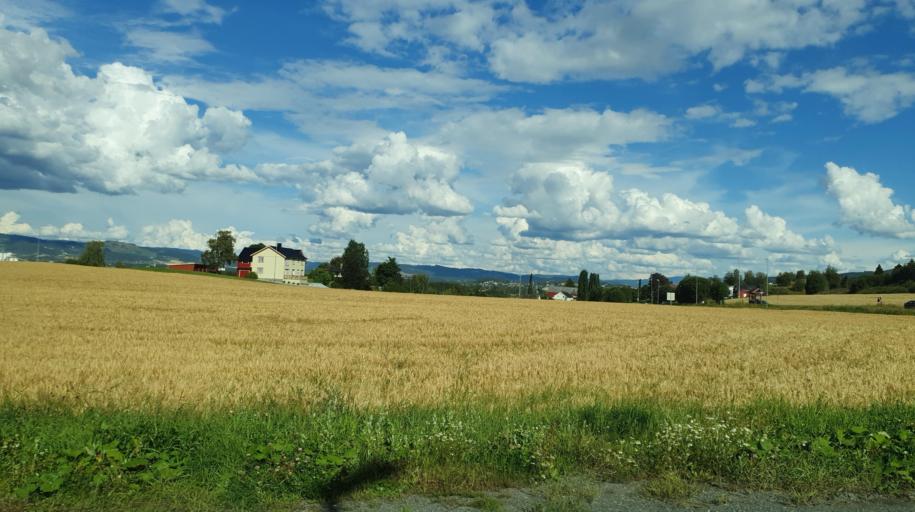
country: NO
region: Nord-Trondelag
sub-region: Verdal
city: Verdal
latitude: 63.7616
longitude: 11.4056
